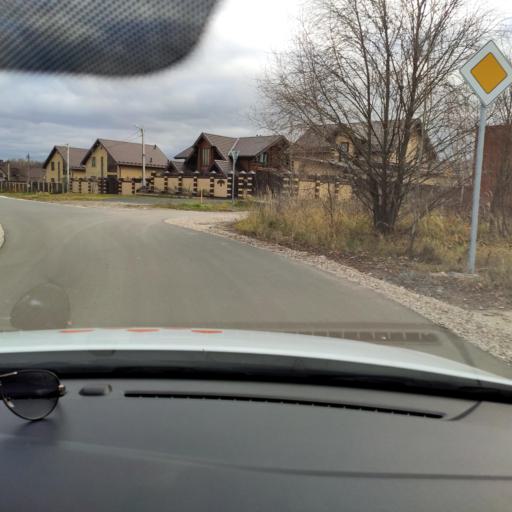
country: RU
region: Tatarstan
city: Stolbishchi
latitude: 55.7372
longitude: 49.2665
